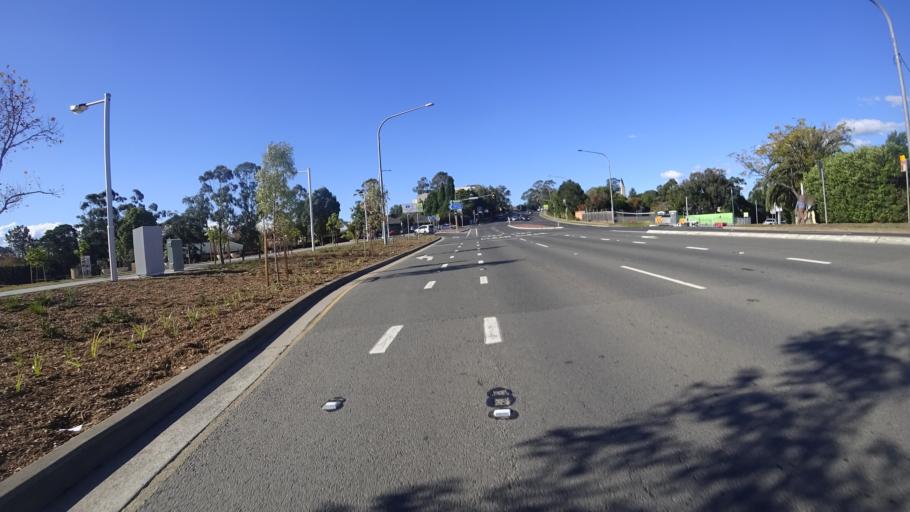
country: AU
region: New South Wales
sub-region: The Hills Shire
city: Castle Hill
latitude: -33.7314
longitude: 151.0089
